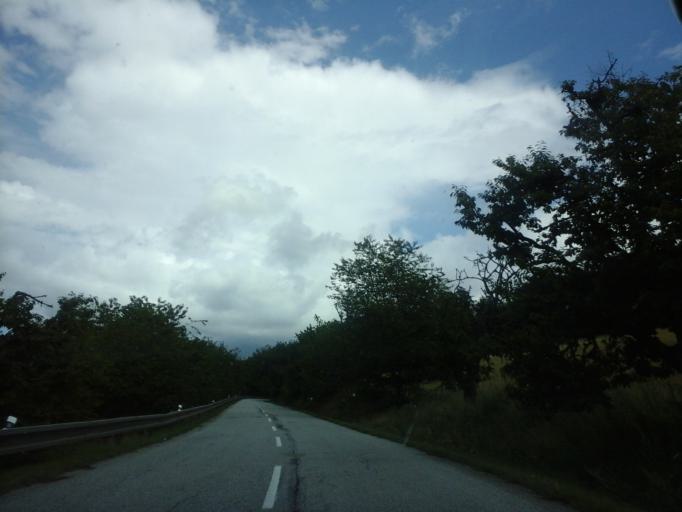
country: SK
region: Kosicky
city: Dobsina
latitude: 48.7095
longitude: 20.3708
